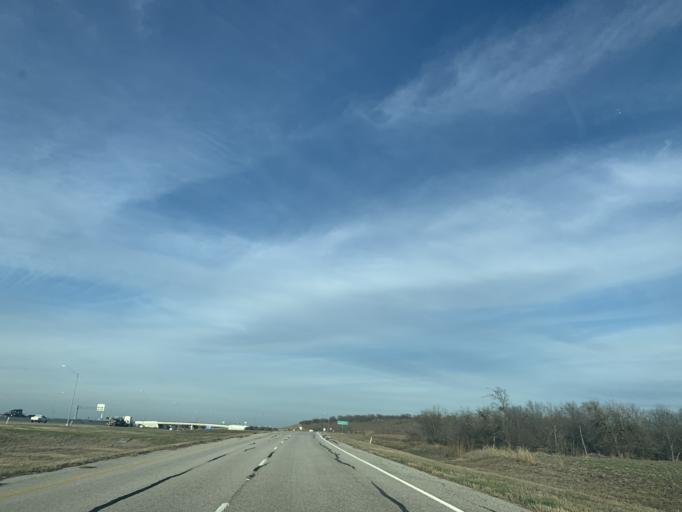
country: US
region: Texas
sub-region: Bell County
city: Salado
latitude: 30.8840
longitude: -97.5754
